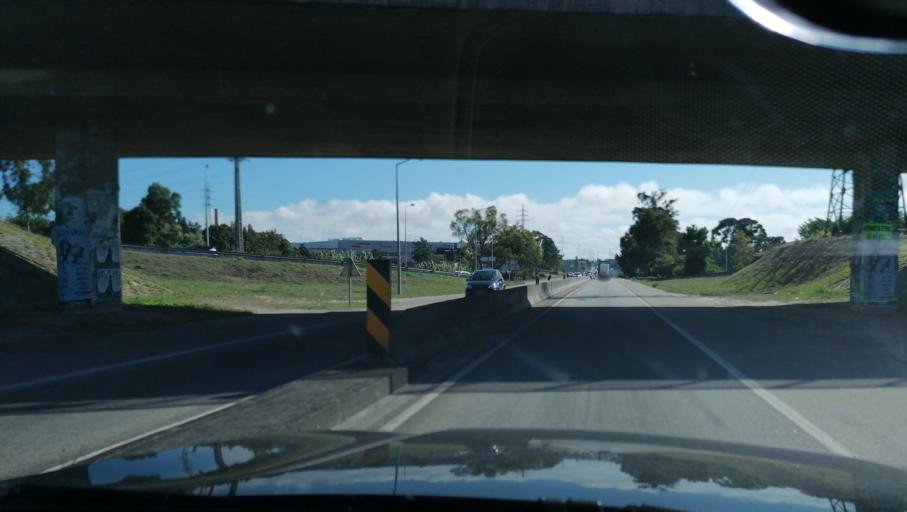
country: PT
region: Aveiro
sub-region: Aveiro
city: Aveiro
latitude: 40.6545
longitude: -8.6191
